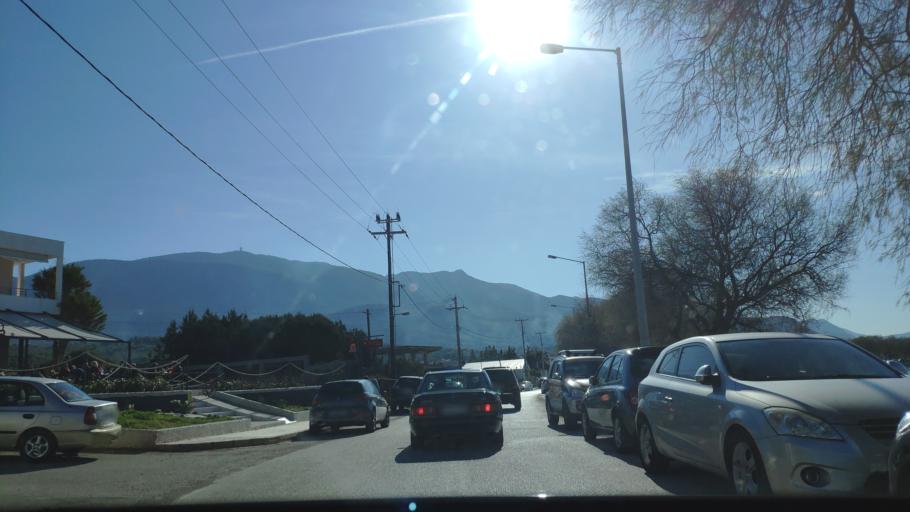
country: GR
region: Attica
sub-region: Nomarchia Dytikis Attikis
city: Kineta
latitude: 38.0740
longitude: 23.1707
